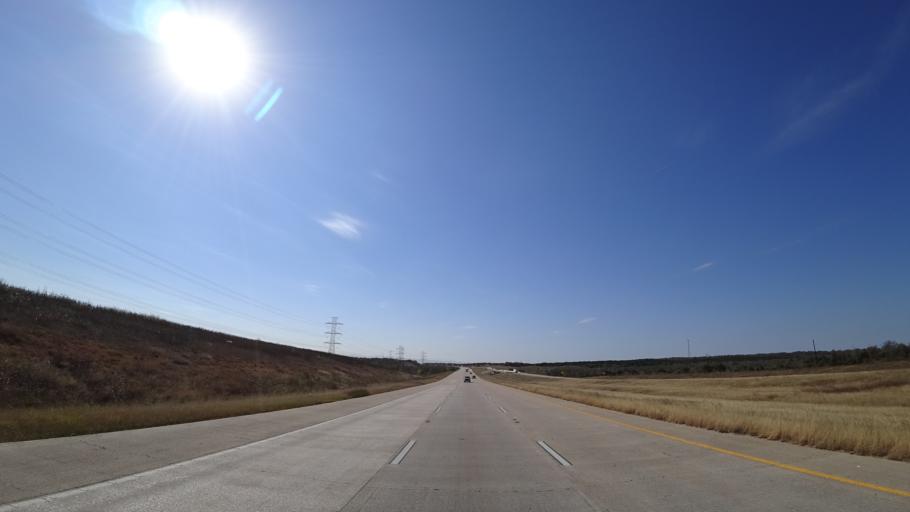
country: US
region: Texas
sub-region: Travis County
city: Hornsby Bend
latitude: 30.2789
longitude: -97.5840
